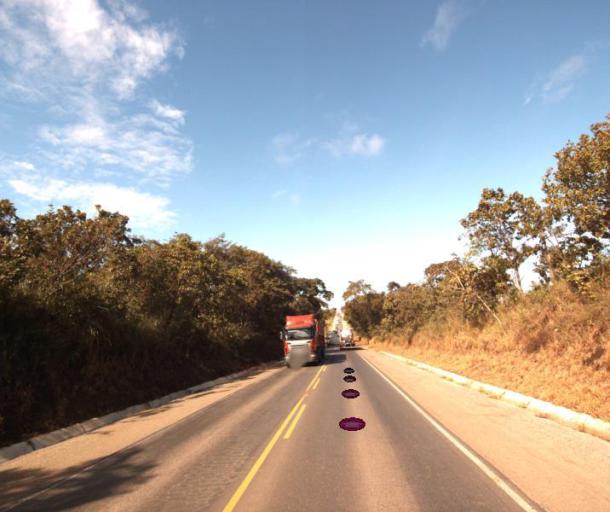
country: BR
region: Goias
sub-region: Itapaci
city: Itapaci
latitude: -14.8465
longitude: -49.3142
